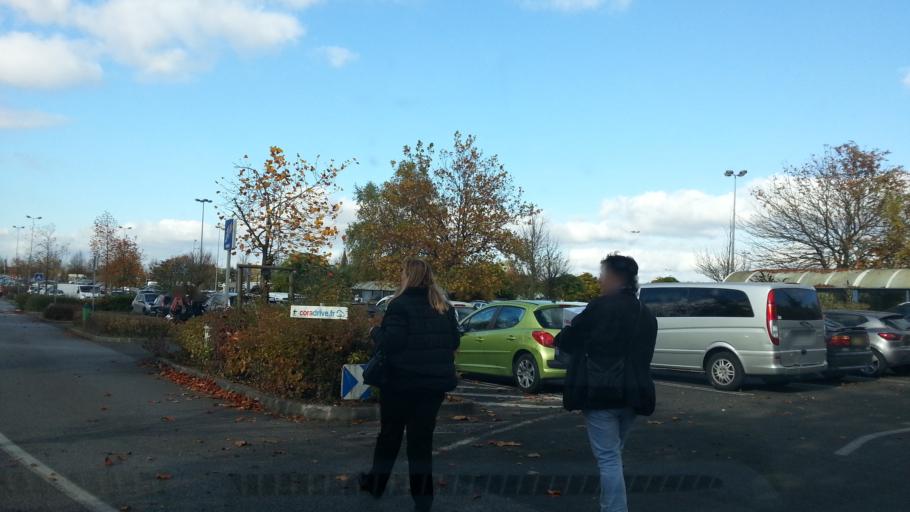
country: FR
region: Picardie
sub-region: Departement de l'Oise
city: Saint-Maximin
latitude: 49.2363
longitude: 2.4717
